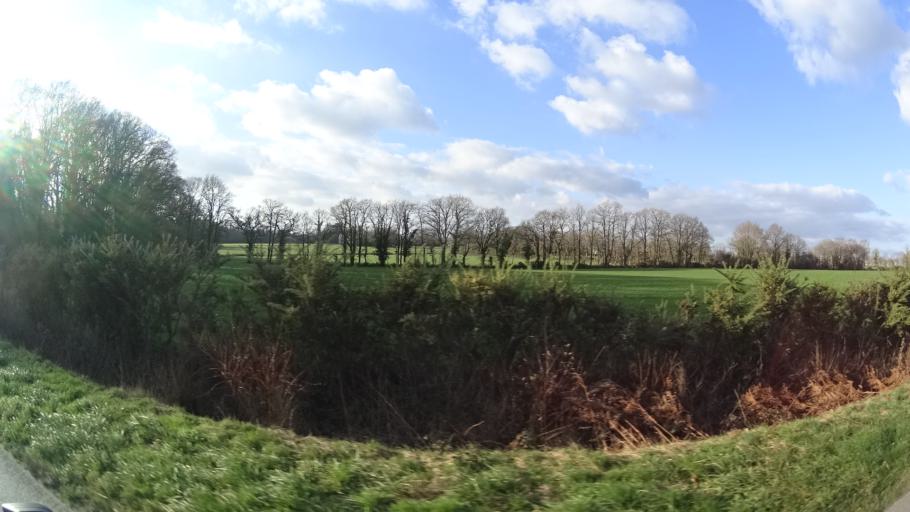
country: FR
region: Pays de la Loire
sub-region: Departement de la Loire-Atlantique
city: Plesse
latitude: 47.5777
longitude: -1.8621
